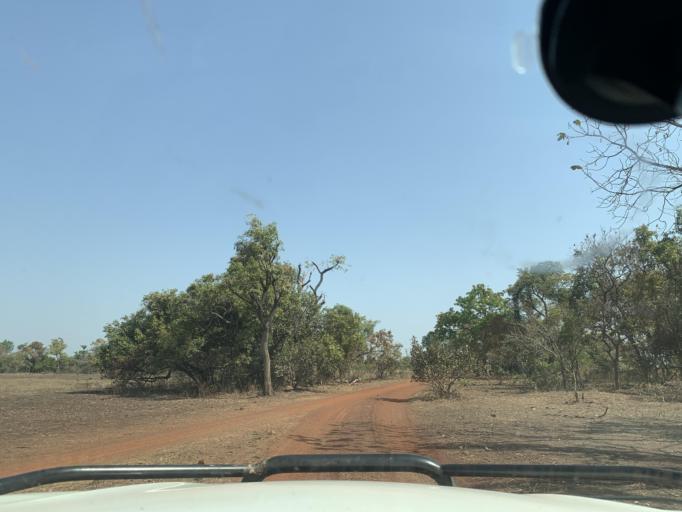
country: ML
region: Sikasso
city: Kolondieba
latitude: 10.8902
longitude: -6.7571
